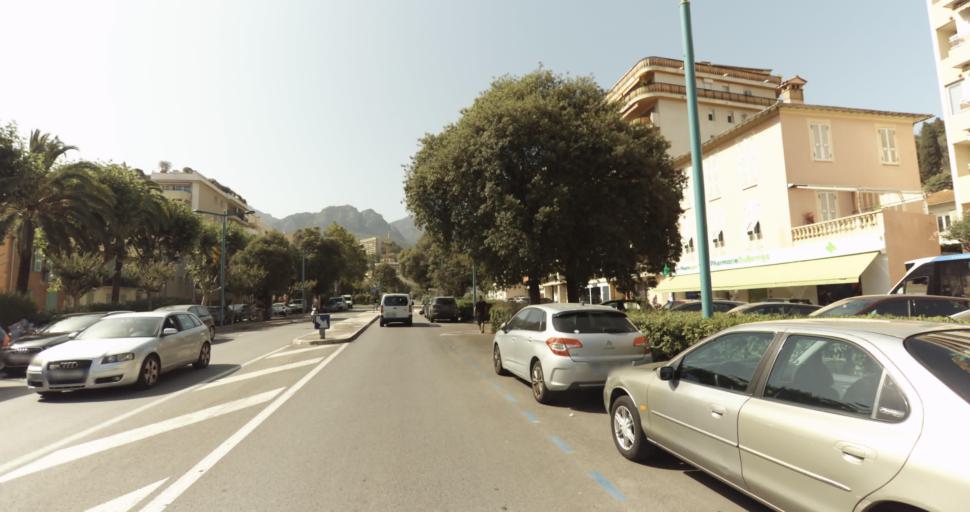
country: FR
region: Provence-Alpes-Cote d'Azur
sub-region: Departement des Alpes-Maritimes
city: Roquebrune-Cap-Martin
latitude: 43.7765
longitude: 7.4879
